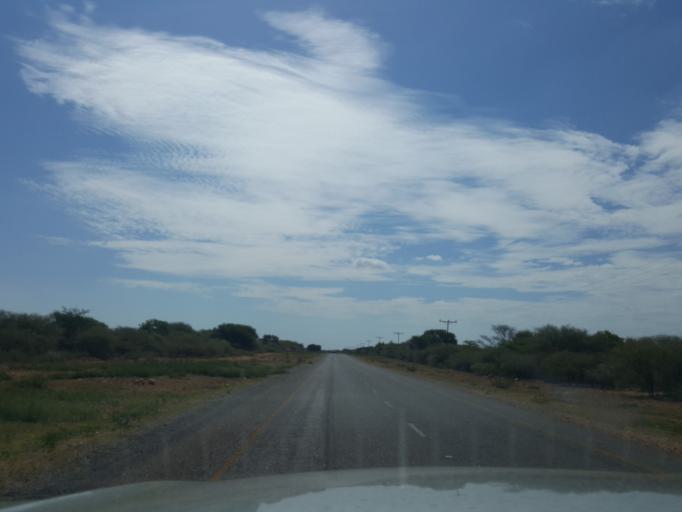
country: BW
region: Kweneng
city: Letlhakeng
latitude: -24.1419
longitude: 25.1460
